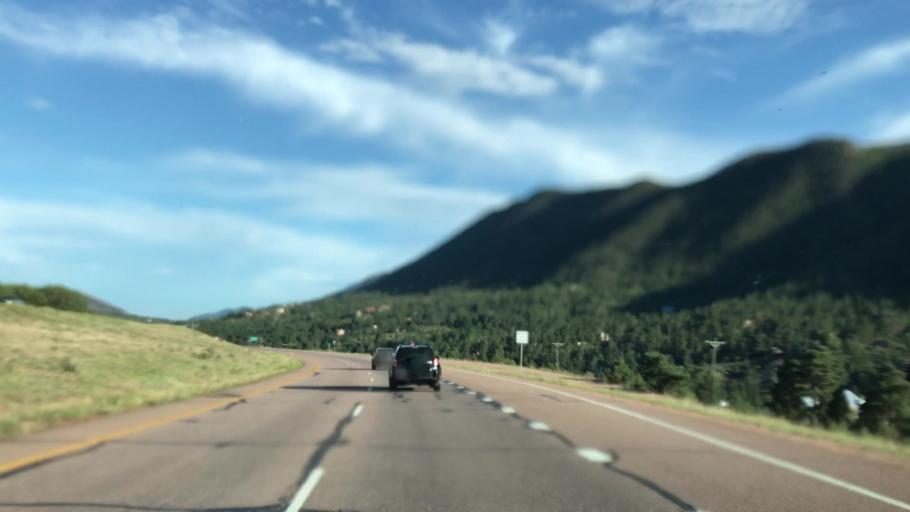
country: US
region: Colorado
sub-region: El Paso County
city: Cascade-Chipita Park
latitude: 38.9272
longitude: -104.9985
